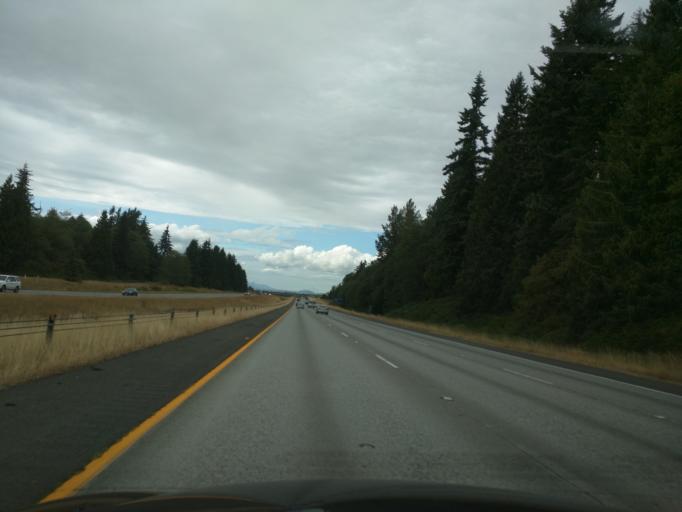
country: US
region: Washington
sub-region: Snohomish County
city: Stanwood
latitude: 48.3006
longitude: -122.3071
